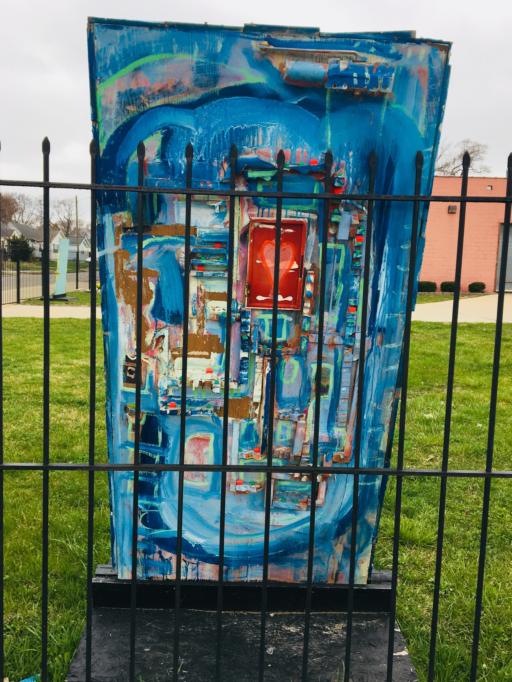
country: US
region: Michigan
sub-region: Macomb County
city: Eastpointe
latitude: 42.4201
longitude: -82.9746
